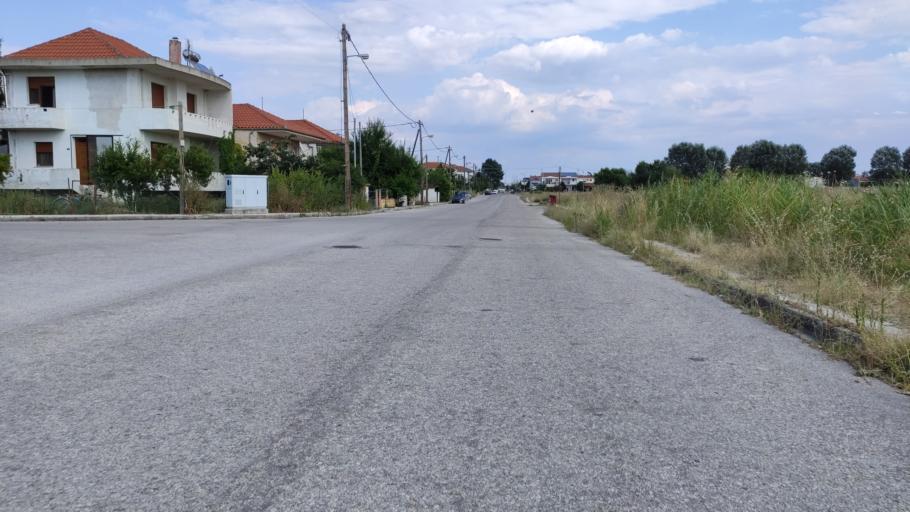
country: GR
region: East Macedonia and Thrace
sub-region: Nomos Rodopis
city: Komotini
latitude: 41.1300
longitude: 25.3929
